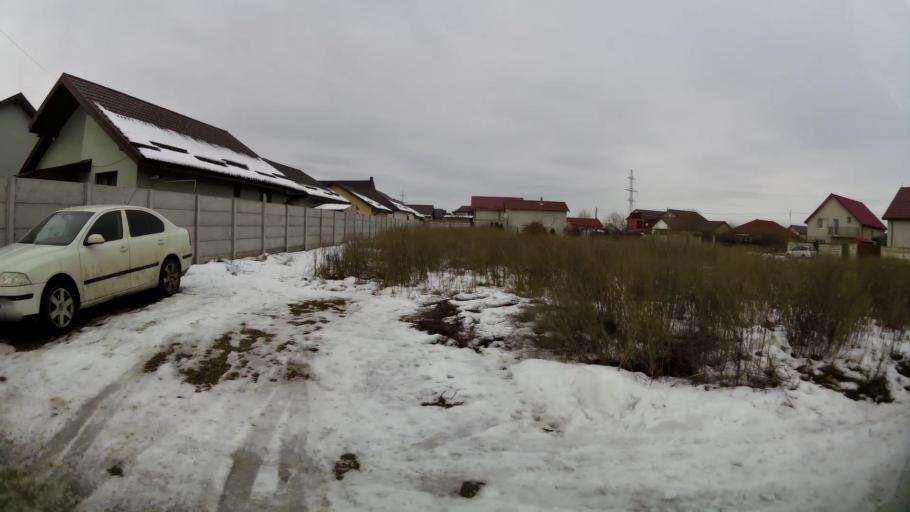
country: RO
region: Ilfov
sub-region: Comuna Pantelimon
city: Pantelimon
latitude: 44.4606
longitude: 26.2013
